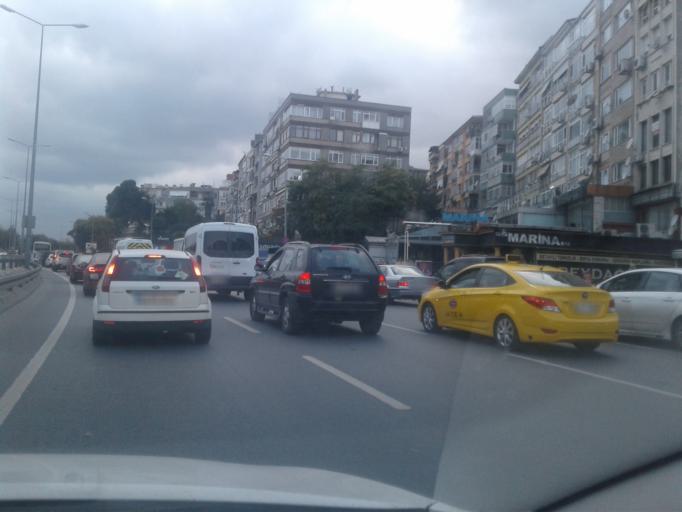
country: TR
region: Istanbul
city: Zeytinburnu
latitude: 40.9770
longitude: 28.8813
